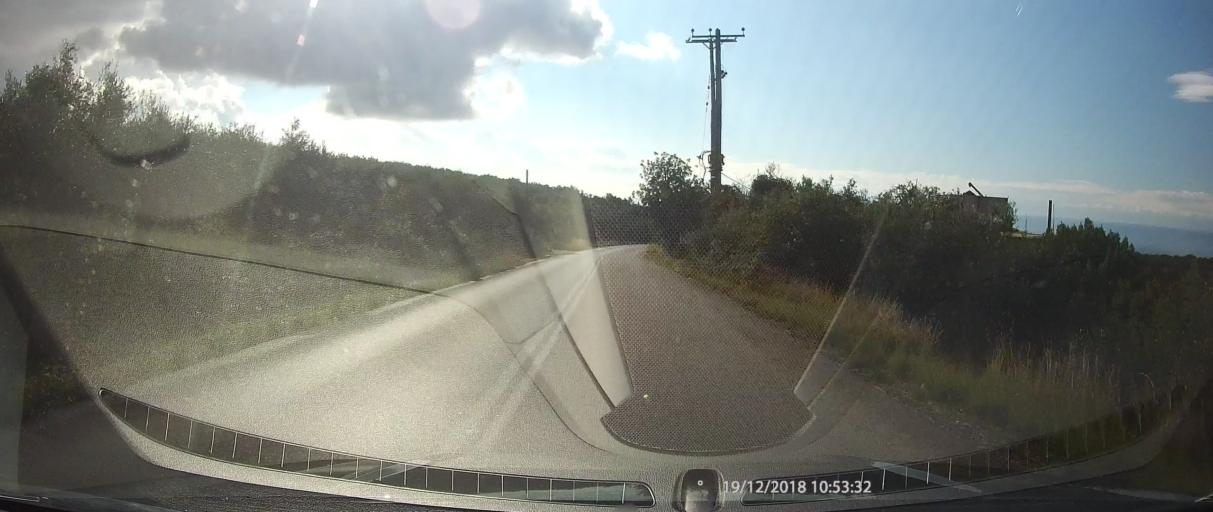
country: GR
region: Peloponnese
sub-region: Nomos Messinias
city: Kardamyli
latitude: 36.9112
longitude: 22.2331
